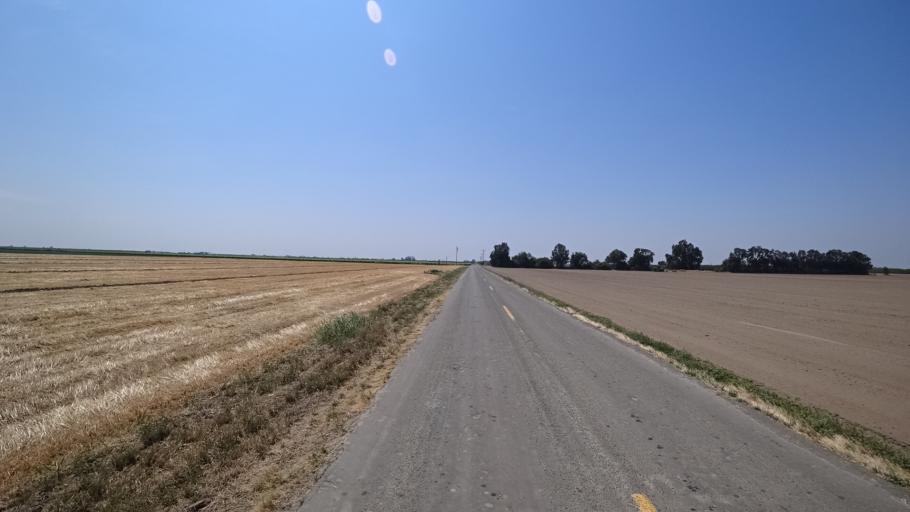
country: US
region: California
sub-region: Kings County
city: Lemoore
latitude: 36.3592
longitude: -119.7629
